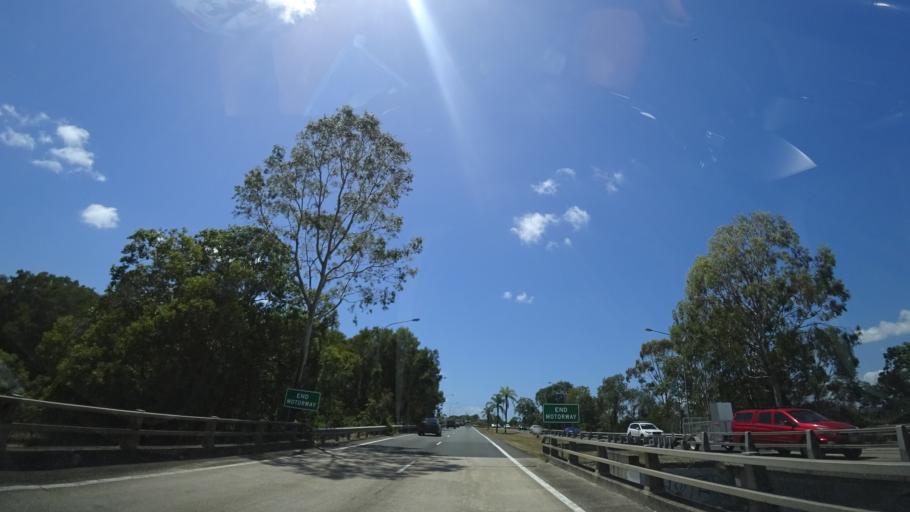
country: AU
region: Queensland
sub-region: Sunshine Coast
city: Mooloolaba
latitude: -26.6968
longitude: 153.1153
